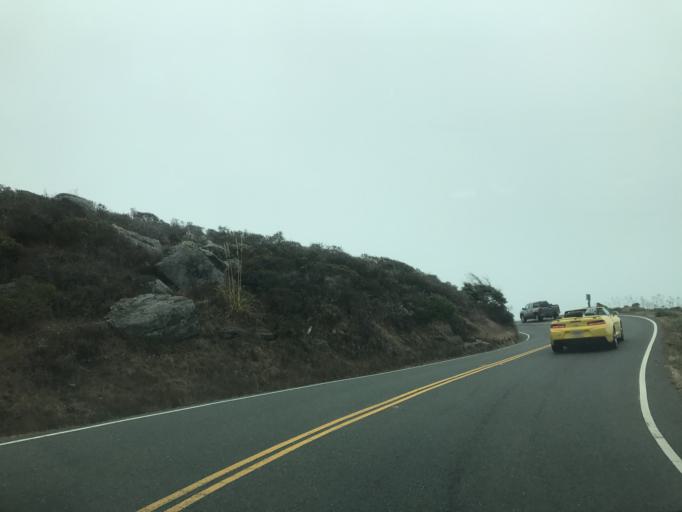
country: US
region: California
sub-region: Sonoma County
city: Monte Rio
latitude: 38.4552
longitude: -123.1329
